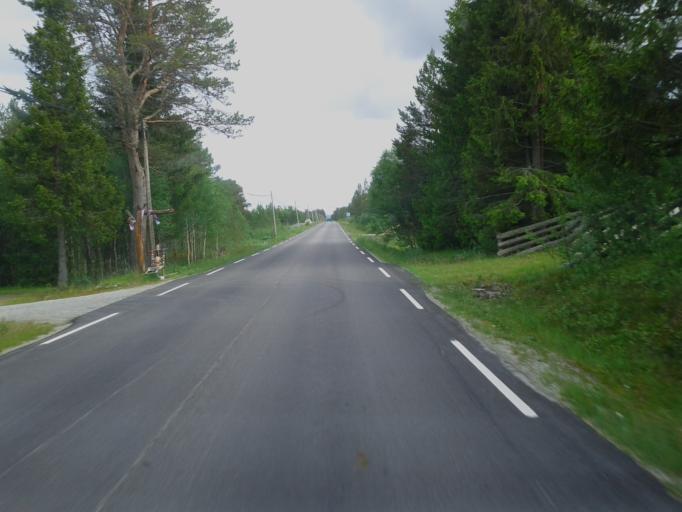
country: NO
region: Sor-Trondelag
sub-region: Roros
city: Roros
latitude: 62.2959
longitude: 11.7265
